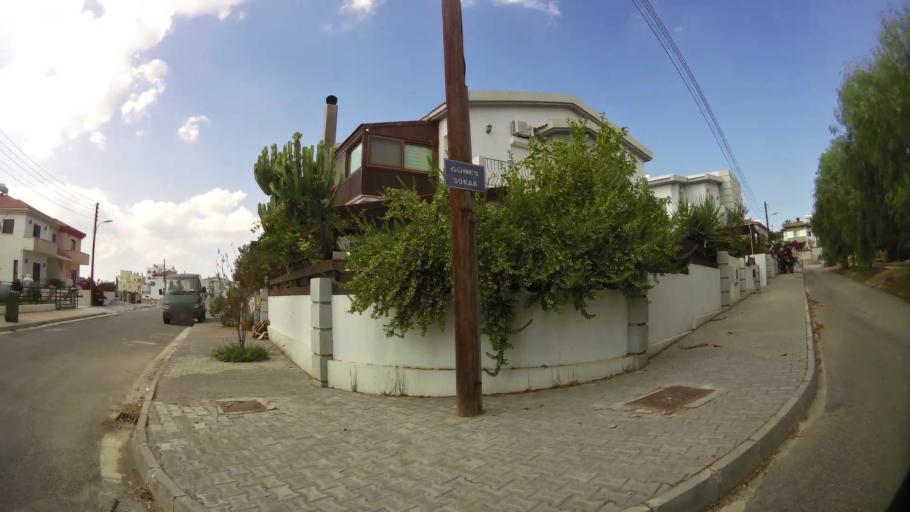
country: CY
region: Lefkosia
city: Nicosia
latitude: 35.2262
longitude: 33.2950
